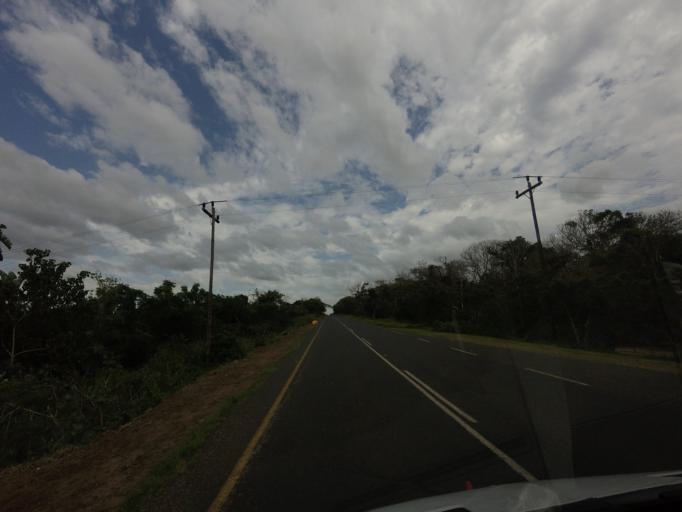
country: ZA
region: KwaZulu-Natal
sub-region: uMkhanyakude District Municipality
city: Mtubatuba
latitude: -28.3742
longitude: 32.3909
